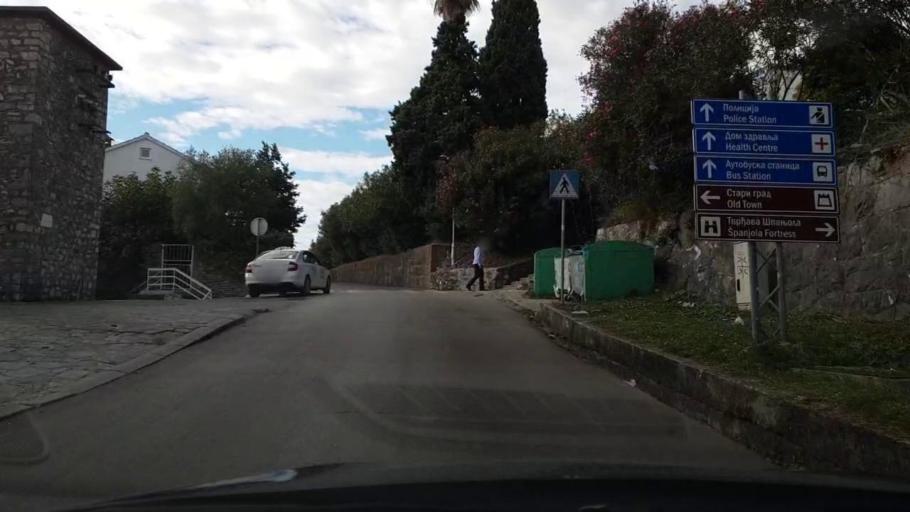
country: ME
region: Herceg Novi
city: Herceg-Novi
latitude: 42.4527
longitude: 18.5383
